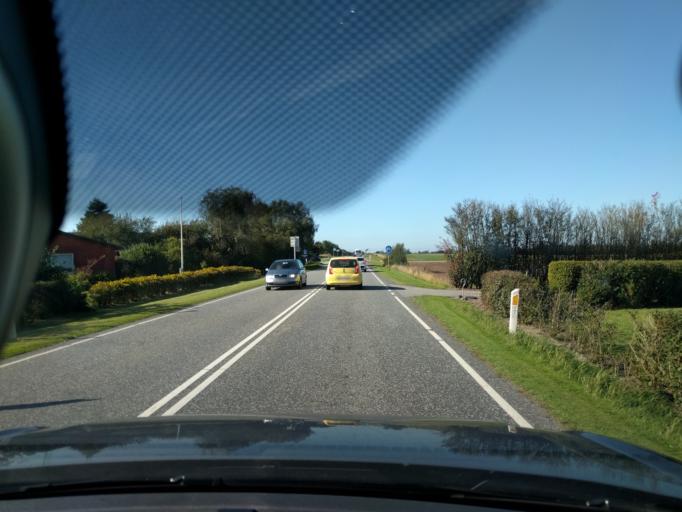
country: DK
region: North Denmark
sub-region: Mariagerfjord Kommune
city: Hobro
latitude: 56.6754
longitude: 9.6752
